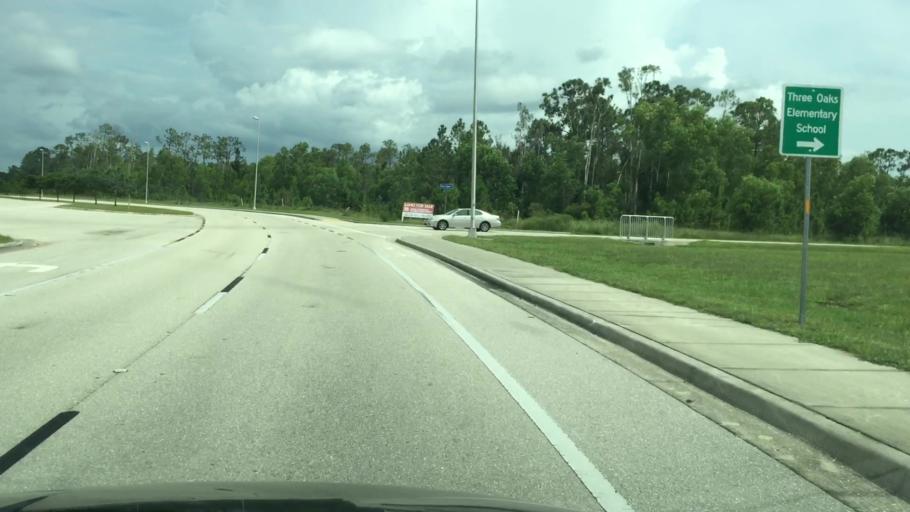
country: US
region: Florida
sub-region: Lee County
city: Three Oaks
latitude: 26.4683
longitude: -81.7933
